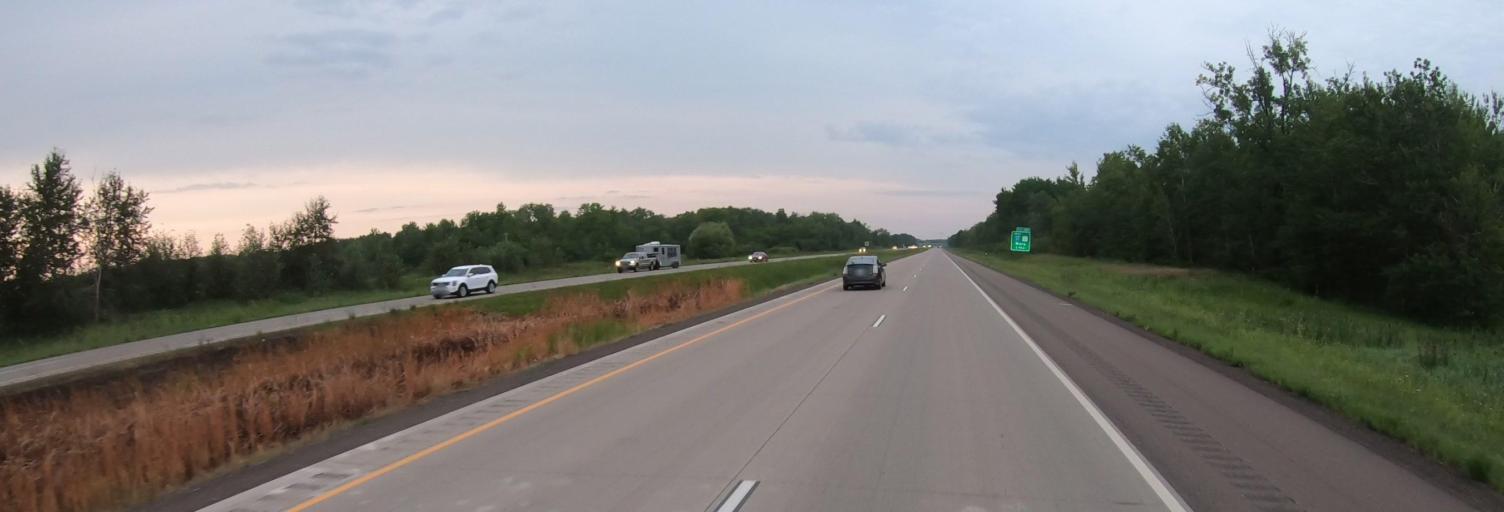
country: US
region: Minnesota
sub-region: Pine County
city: Hinckley
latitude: 45.9606
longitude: -92.9598
